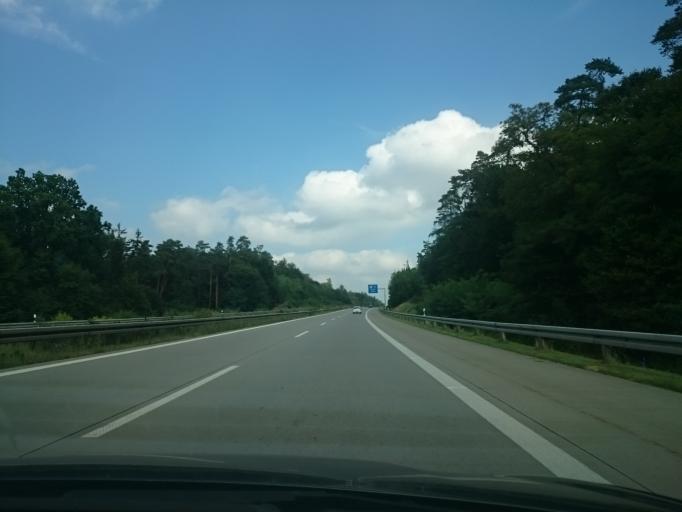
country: DE
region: Brandenburg
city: Rudnitz
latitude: 52.7643
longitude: 13.5510
